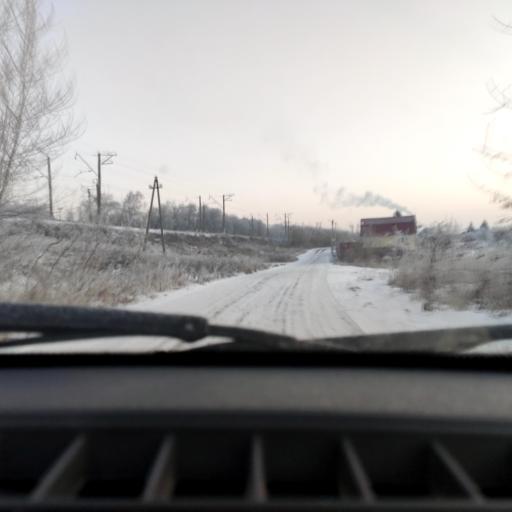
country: RU
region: Bashkortostan
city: Avdon
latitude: 54.6381
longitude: 55.7290
